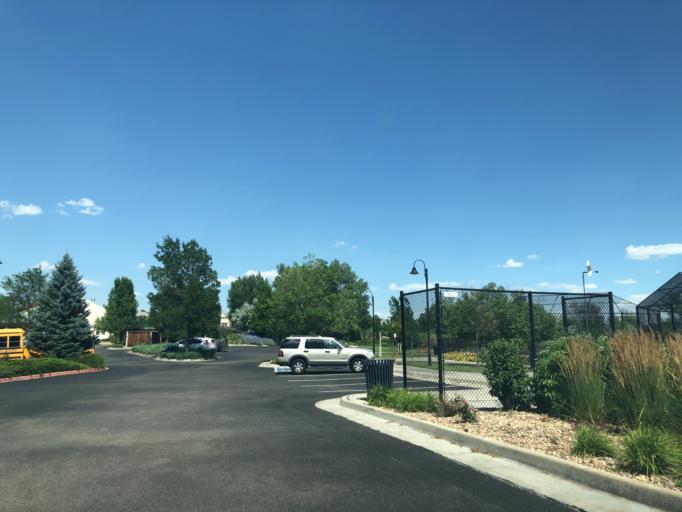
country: US
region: Colorado
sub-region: Arapahoe County
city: Dove Valley
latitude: 39.6045
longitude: -104.7749
